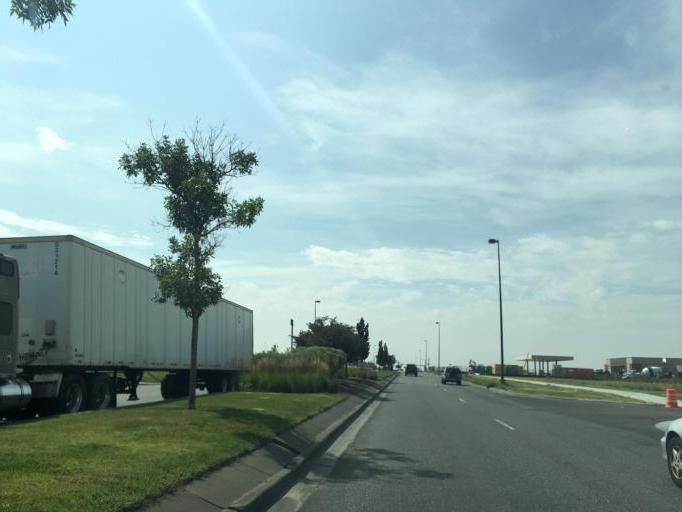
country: US
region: Colorado
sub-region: Adams County
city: Aurora
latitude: 39.8169
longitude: -104.7721
